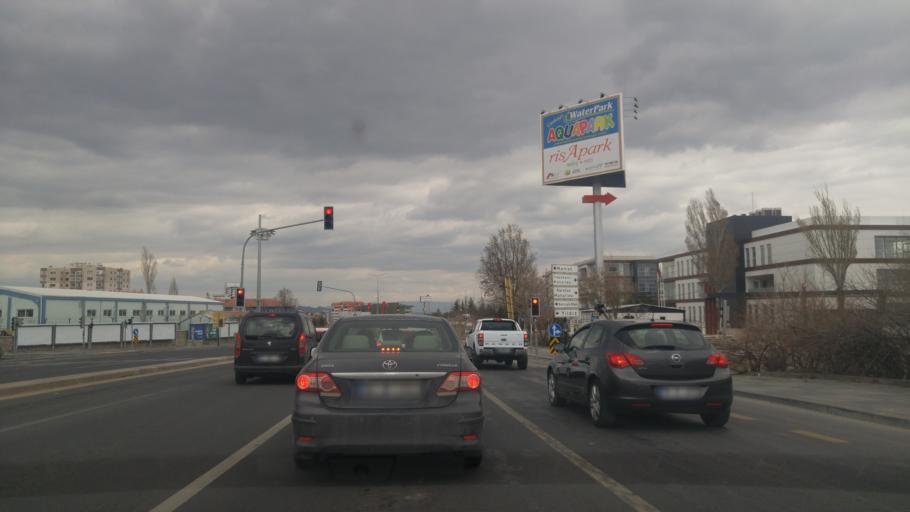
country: TR
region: Ankara
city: Cankaya
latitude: 39.8674
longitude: 32.8689
